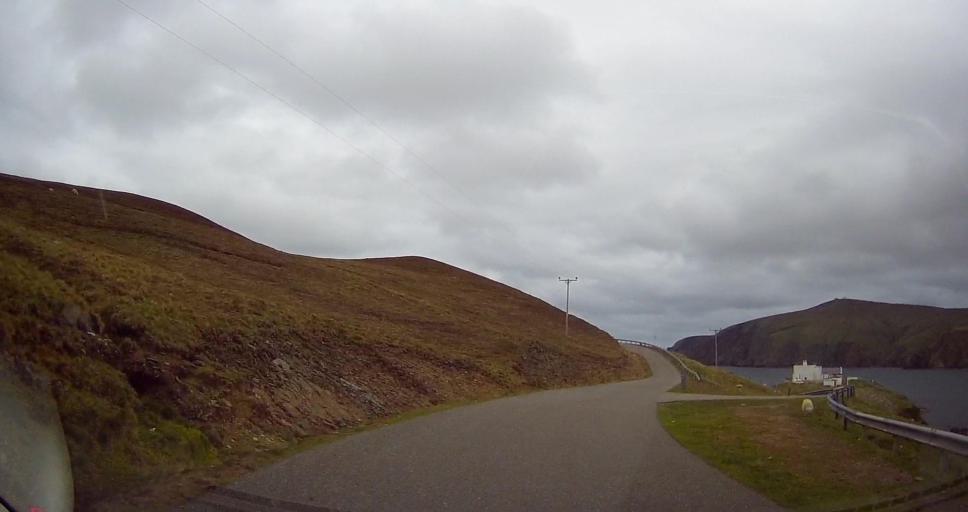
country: GB
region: Scotland
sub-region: Shetland Islands
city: Shetland
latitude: 60.8099
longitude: -0.8780
